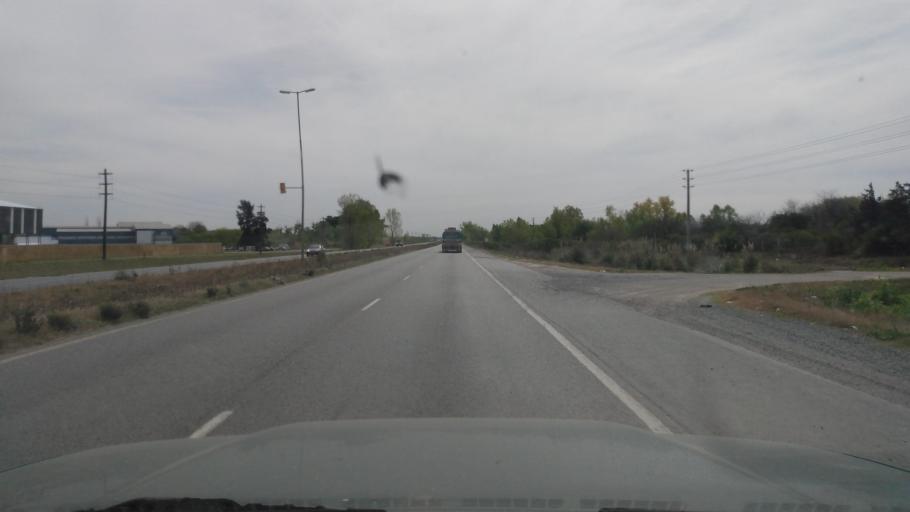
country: AR
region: Buenos Aires
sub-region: Partido de Lujan
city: Lujan
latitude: -34.5517
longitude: -59.0366
